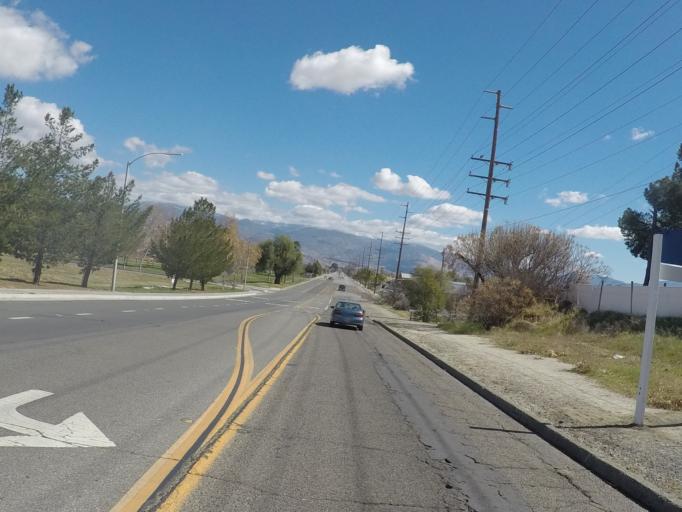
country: US
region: California
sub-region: Riverside County
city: San Jacinto
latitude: 33.7729
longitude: -116.9797
